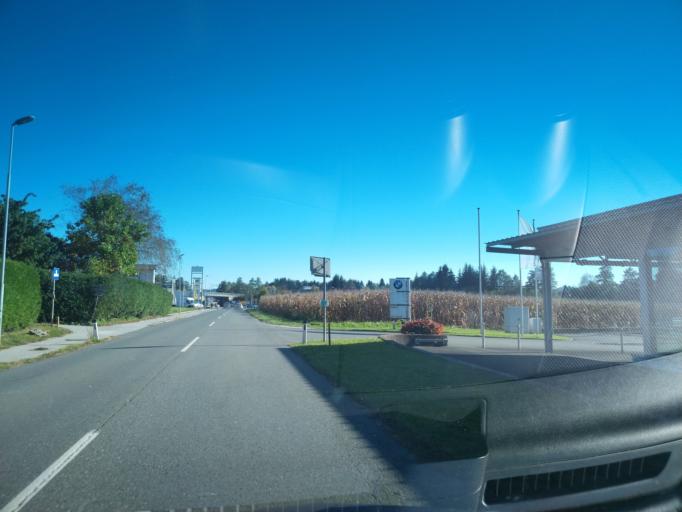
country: AT
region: Styria
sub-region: Politischer Bezirk Deutschlandsberg
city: Stainz
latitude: 46.9003
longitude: 15.2683
